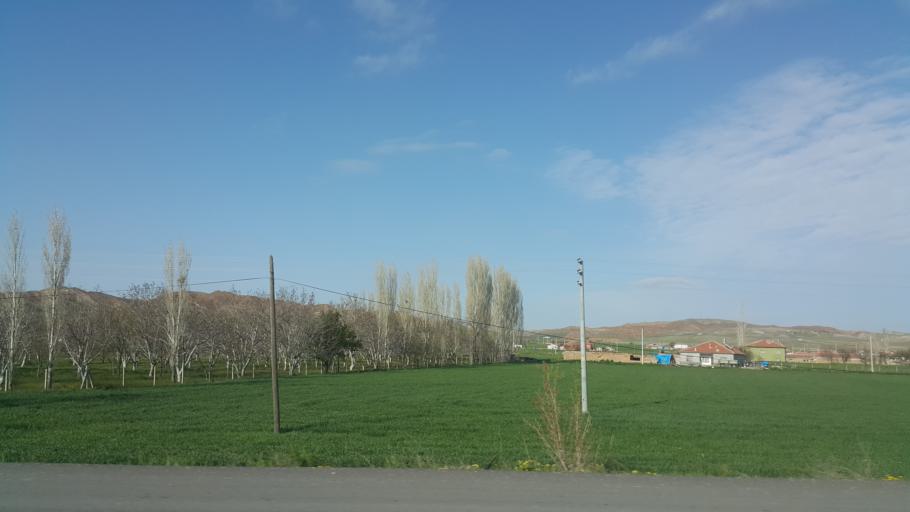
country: TR
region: Aksaray
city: Acipinar
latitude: 38.5083
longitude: 33.8596
